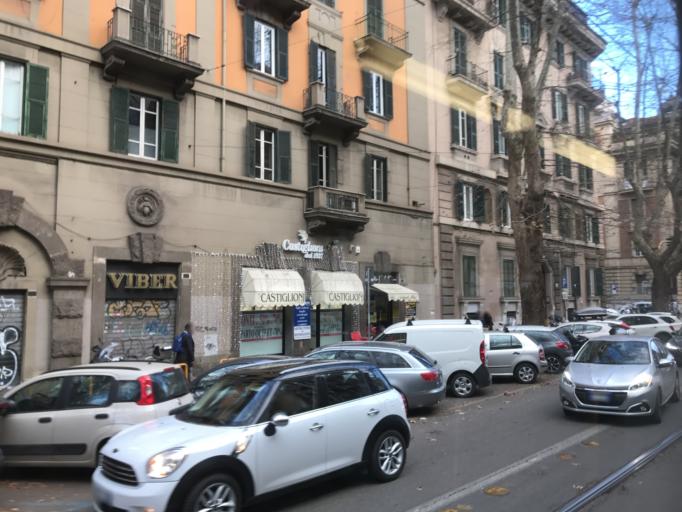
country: IT
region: Latium
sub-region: Citta metropolitana di Roma Capitale
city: Rome
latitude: 41.9151
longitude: 12.5041
